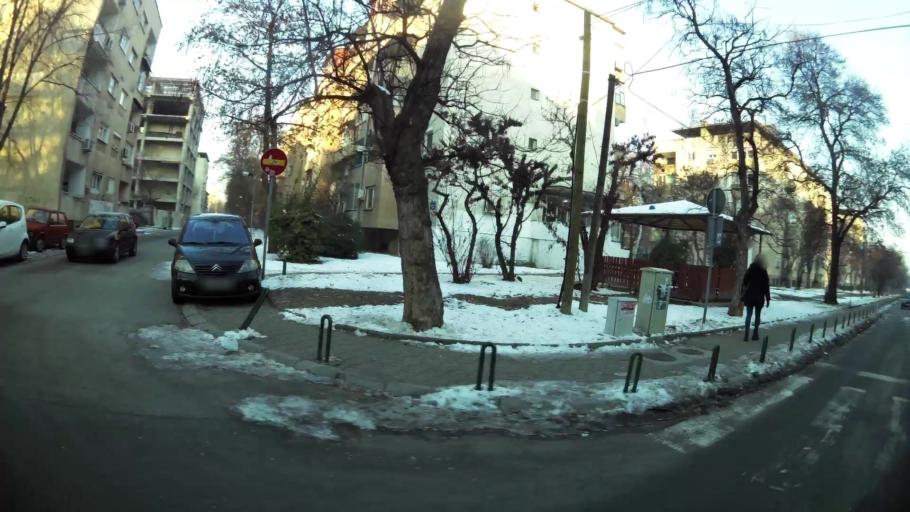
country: MK
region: Karpos
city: Skopje
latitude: 42.0022
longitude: 21.4102
